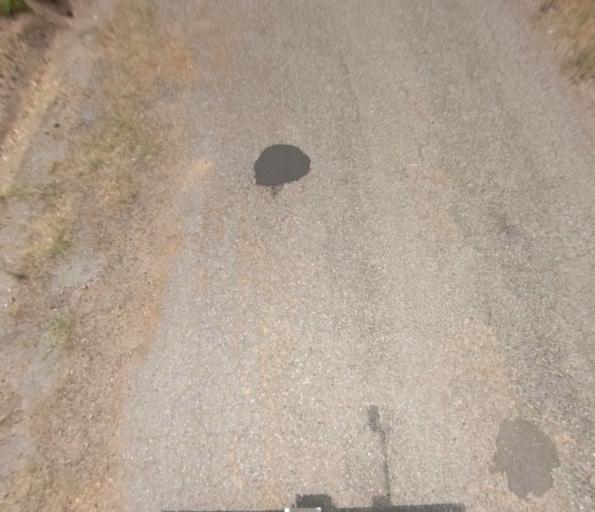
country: US
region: California
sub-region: Madera County
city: Ahwahnee
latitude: 37.3502
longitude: -119.7425
